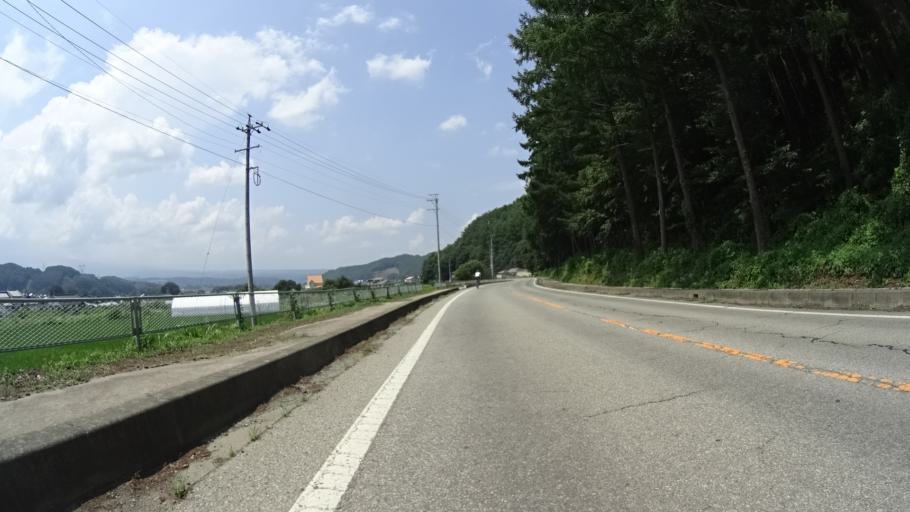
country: JP
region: Nagano
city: Saku
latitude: 36.1483
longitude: 138.5127
